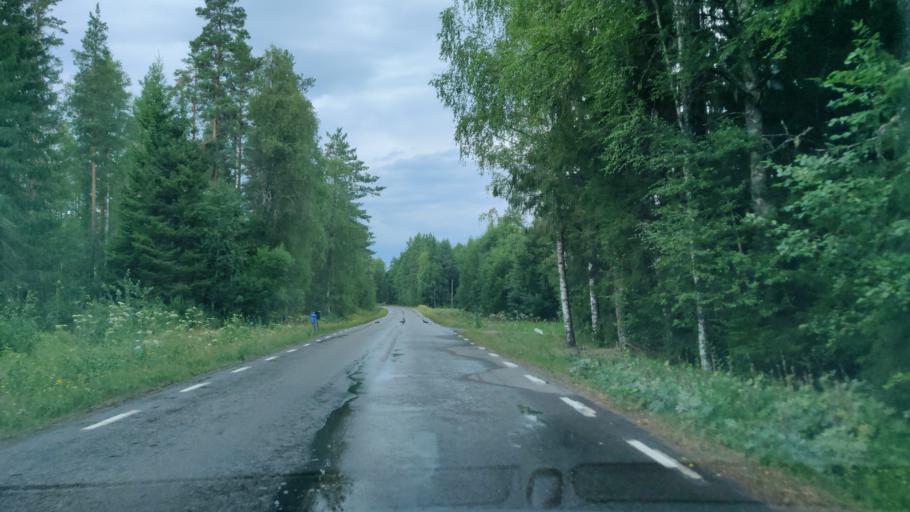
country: SE
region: Vaermland
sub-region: Munkfors Kommun
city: Munkfors
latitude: 59.8776
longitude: 13.5225
